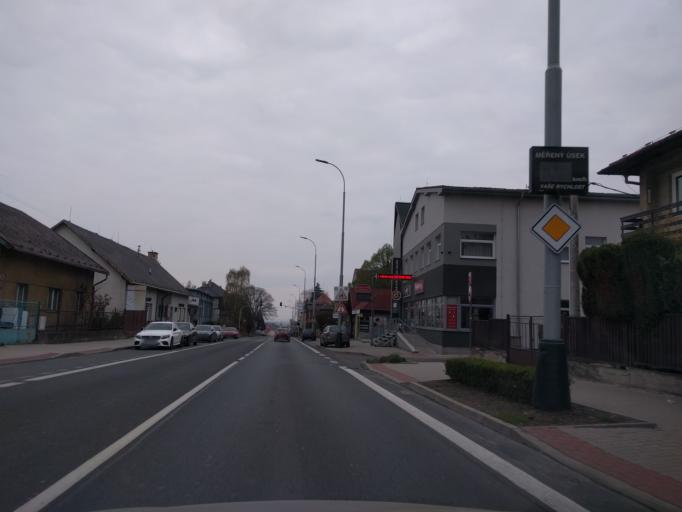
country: CZ
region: Central Bohemia
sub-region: Okres Praha-Vychod
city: Ricany
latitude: 49.9980
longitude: 14.6718
